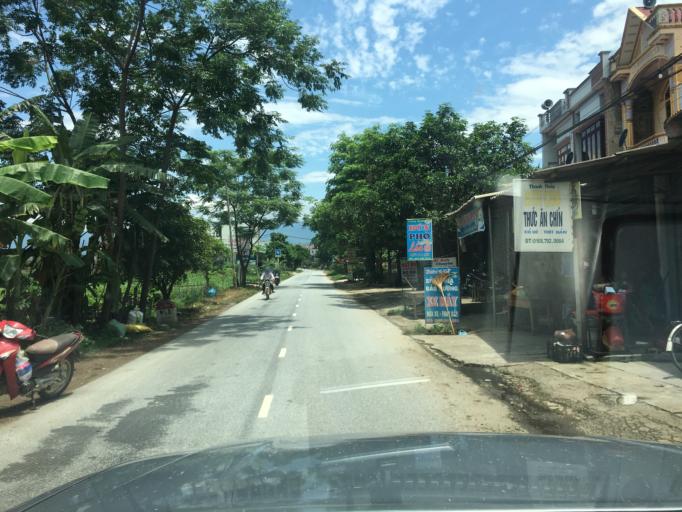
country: VN
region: Yen Bai
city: Son Thinh
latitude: 21.6434
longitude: 104.5004
